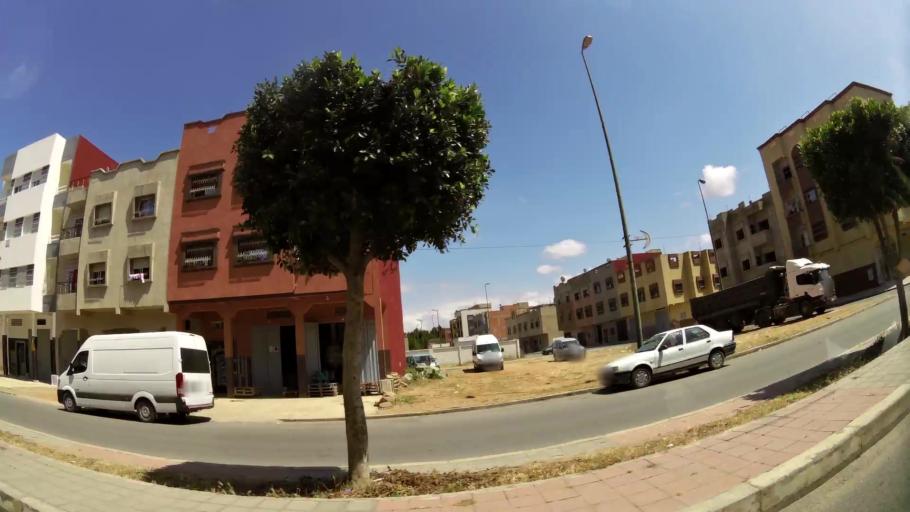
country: MA
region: Gharb-Chrarda-Beni Hssen
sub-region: Kenitra Province
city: Kenitra
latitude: 34.2460
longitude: -6.5368
